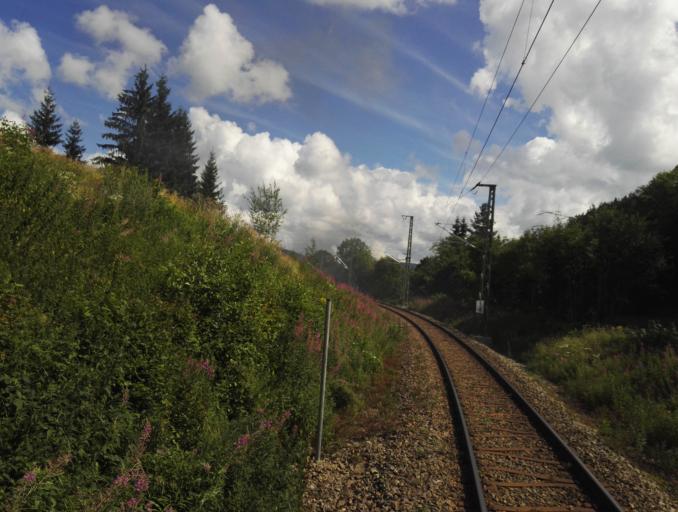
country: DE
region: Baden-Wuerttemberg
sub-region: Freiburg Region
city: Titisee-Neustadt
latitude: 47.9018
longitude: 8.1651
